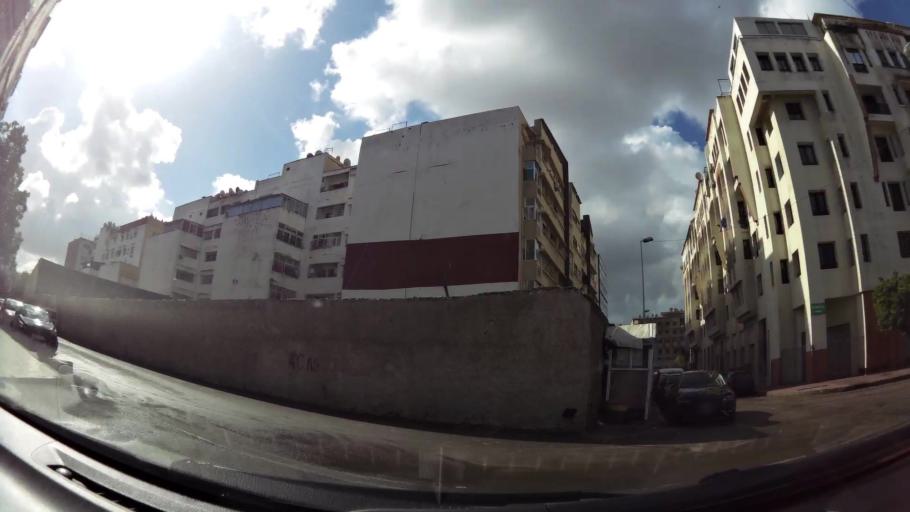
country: MA
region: Grand Casablanca
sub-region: Casablanca
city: Casablanca
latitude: 33.5708
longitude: -7.6276
